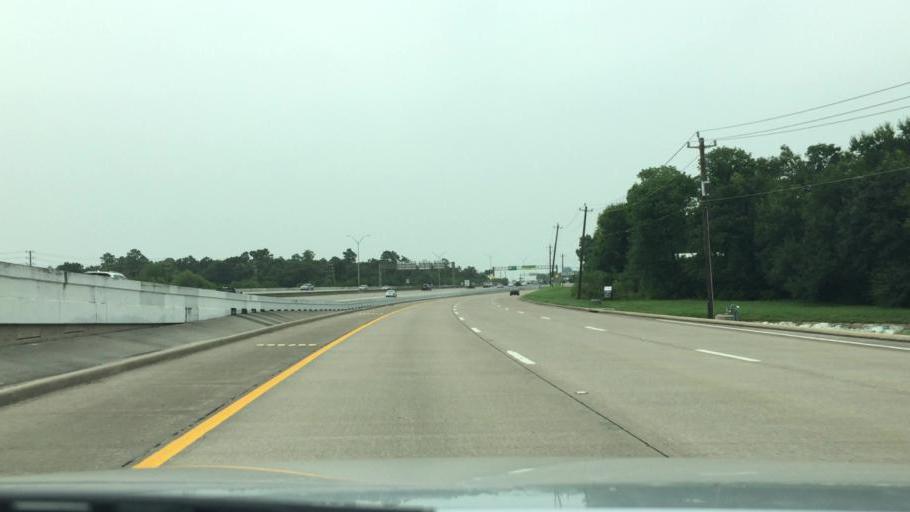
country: US
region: Texas
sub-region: Harris County
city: Cloverleaf
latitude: 29.7775
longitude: -95.1575
